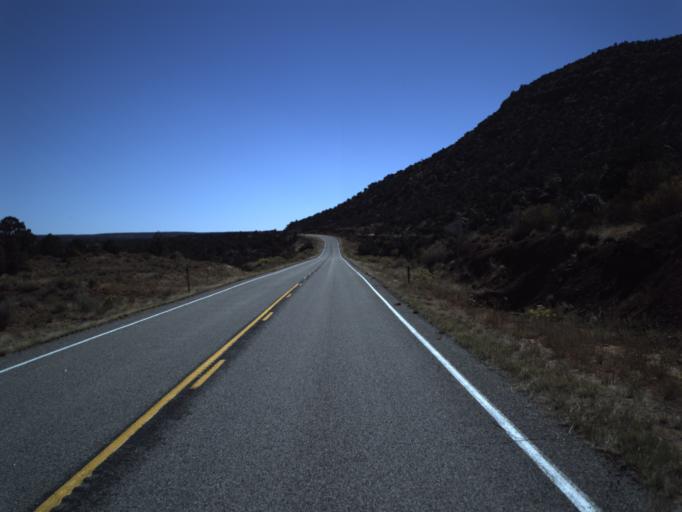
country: US
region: Utah
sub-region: San Juan County
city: Blanding
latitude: 37.6016
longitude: -110.0590
